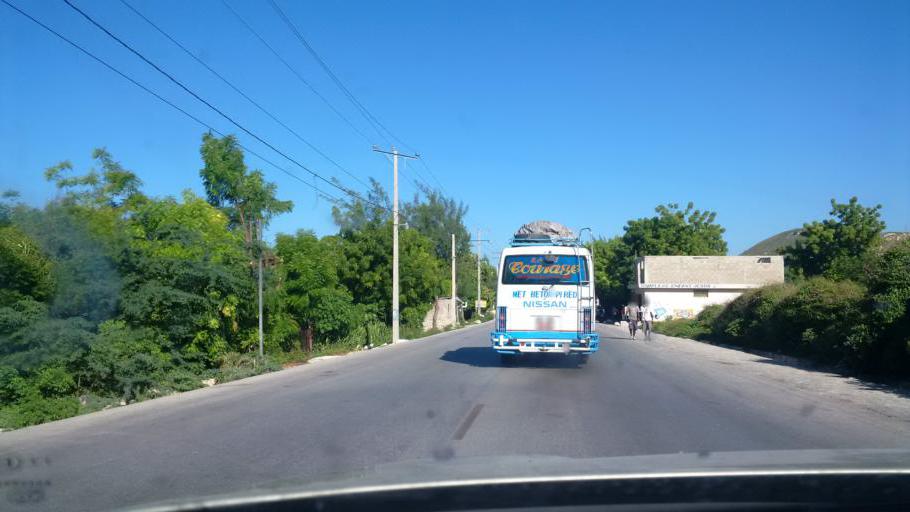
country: HT
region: Ouest
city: Cabaret
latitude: 18.7170
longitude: -72.3660
